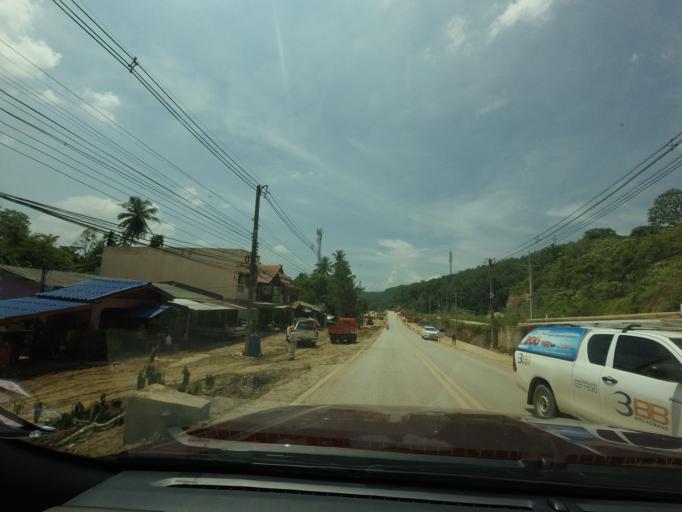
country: TH
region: Yala
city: Betong
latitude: 5.8049
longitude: 101.0730
